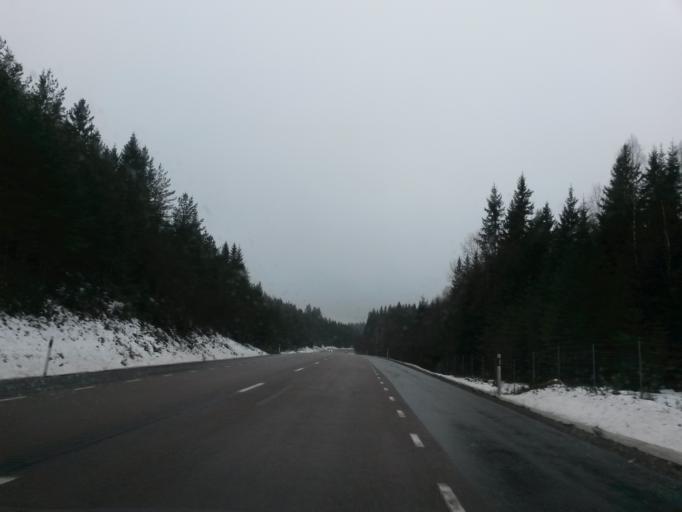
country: SE
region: Vaestra Goetaland
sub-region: Boras Kommun
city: Viskafors
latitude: 57.6207
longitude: 12.8839
